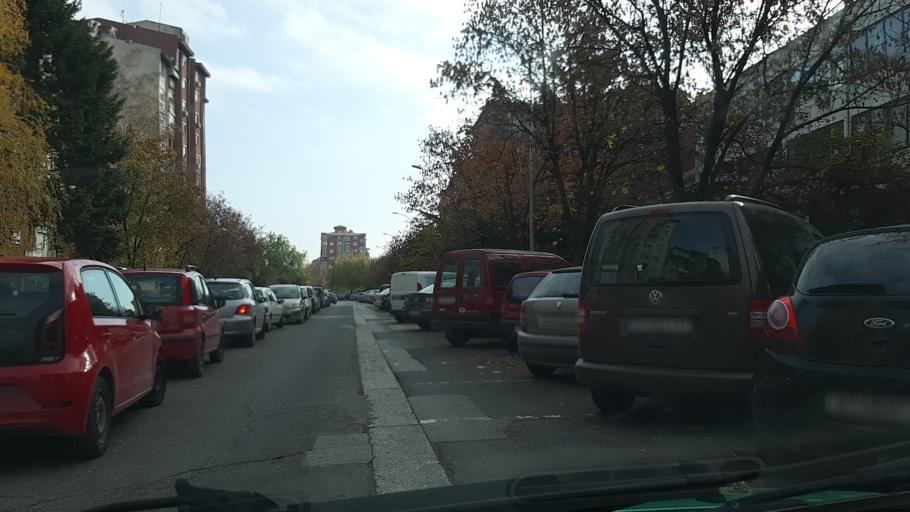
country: MK
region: Kisela Voda
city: Usje
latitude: 41.9844
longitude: 21.4696
